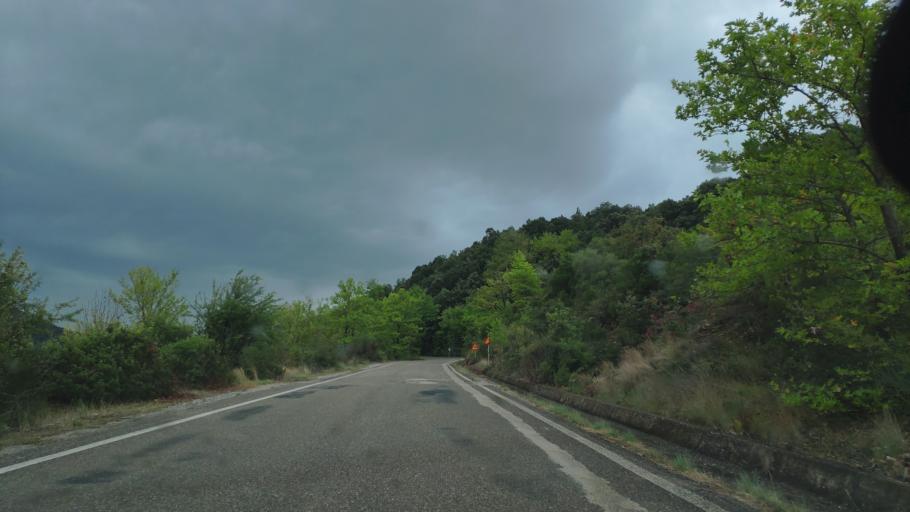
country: GR
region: West Greece
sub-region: Nomos Aitolias kai Akarnanias
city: Lepenou
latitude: 38.8102
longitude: 21.3337
